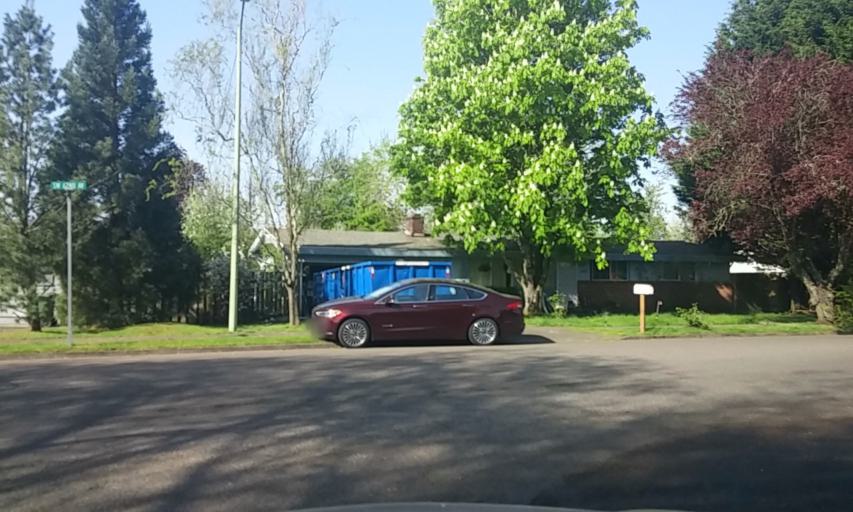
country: US
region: Oregon
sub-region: Washington County
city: Metzger
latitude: 45.4327
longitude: -122.7402
